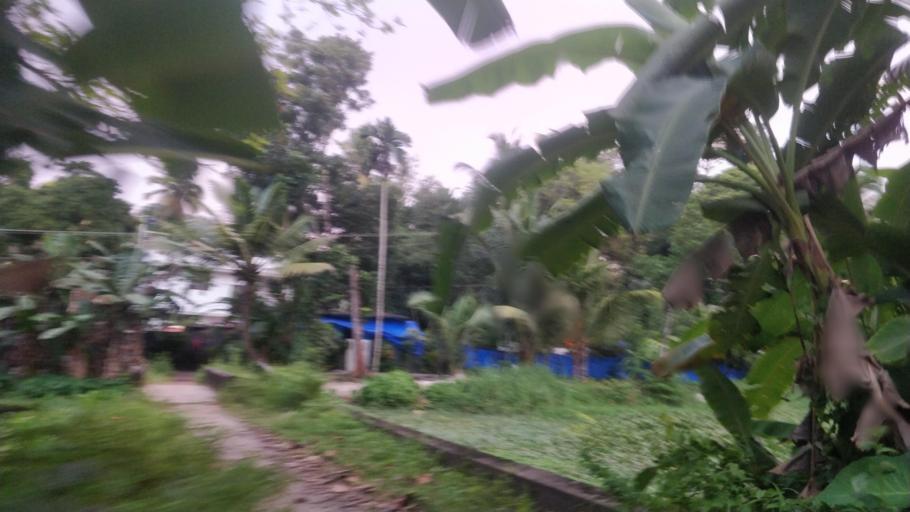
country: IN
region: Kerala
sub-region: Alappuzha
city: Shertallai
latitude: 9.6760
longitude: 76.3346
